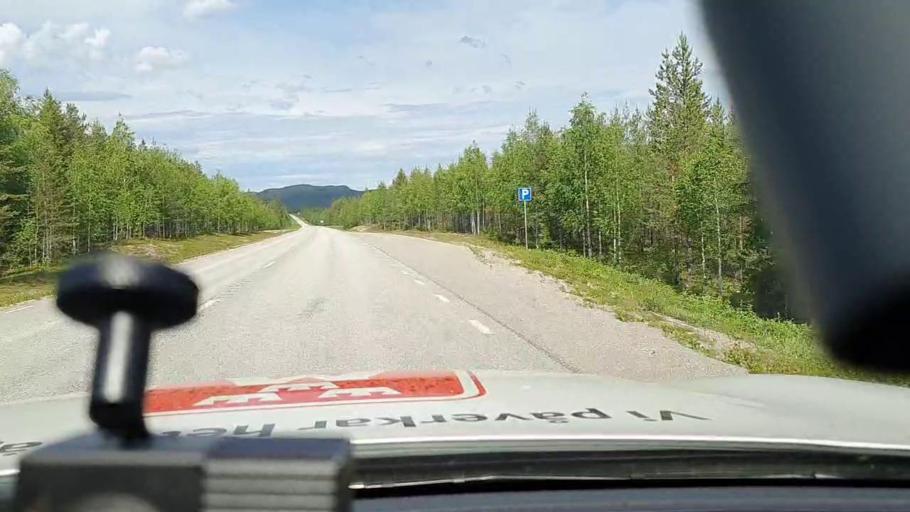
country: SE
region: Norrbotten
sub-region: Jokkmokks Kommun
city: Jokkmokk
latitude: 66.5433
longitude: 20.1399
